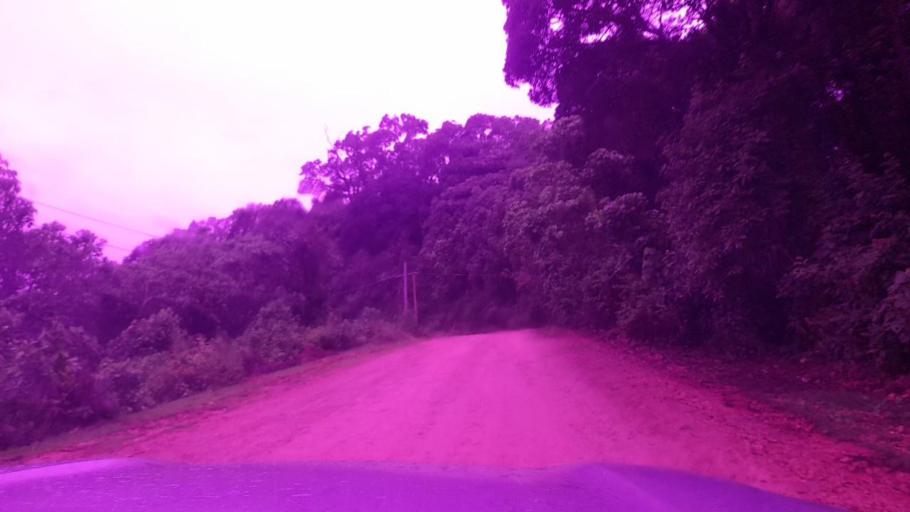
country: ET
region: Southern Nations, Nationalities, and People's Region
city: Bonga
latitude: 7.5065
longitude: 36.0968
